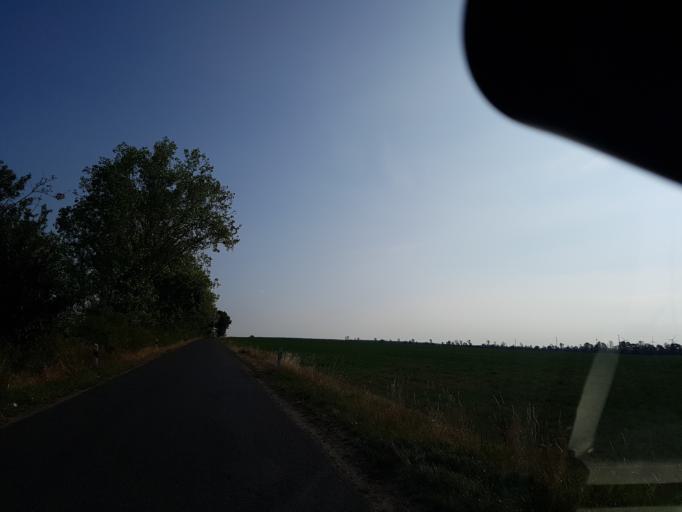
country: DE
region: Saxony-Anhalt
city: Kropstadt
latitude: 52.0246
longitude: 12.7506
